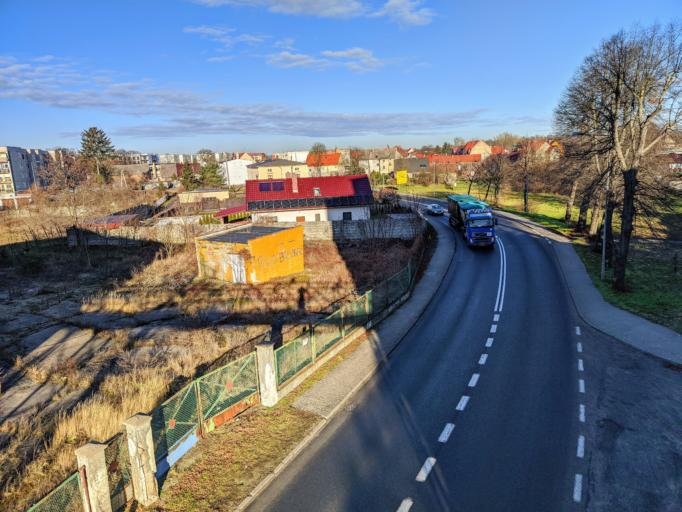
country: PL
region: Lubusz
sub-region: Powiat zielonogorski
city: Nowogrod Bobrzanski
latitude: 51.7951
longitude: 15.2342
